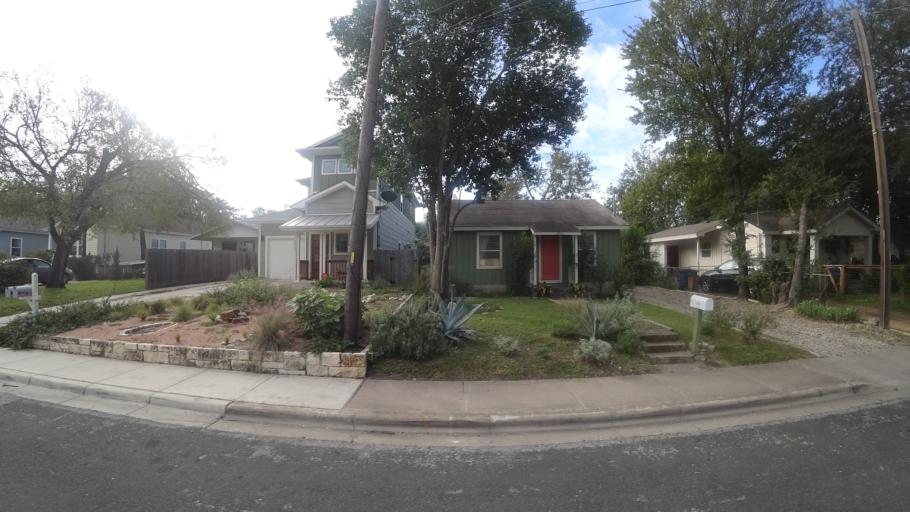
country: US
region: Texas
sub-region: Travis County
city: Austin
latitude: 30.2776
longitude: -97.7081
